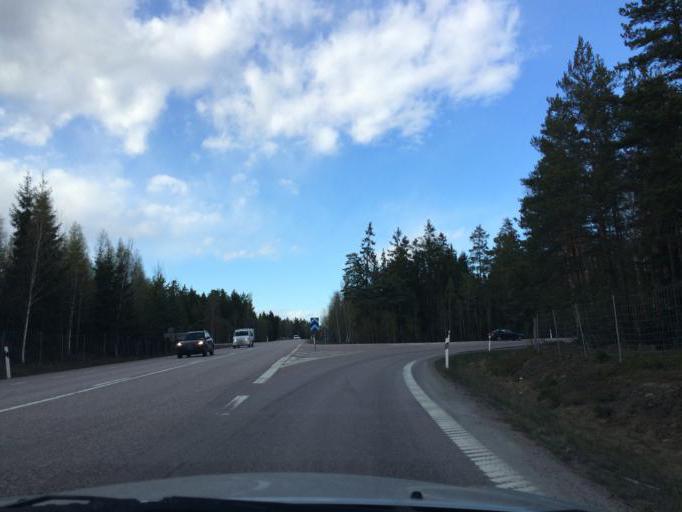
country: SE
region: Vaestmanland
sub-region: Hallstahammars Kommun
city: Kolback
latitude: 59.5784
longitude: 16.3530
